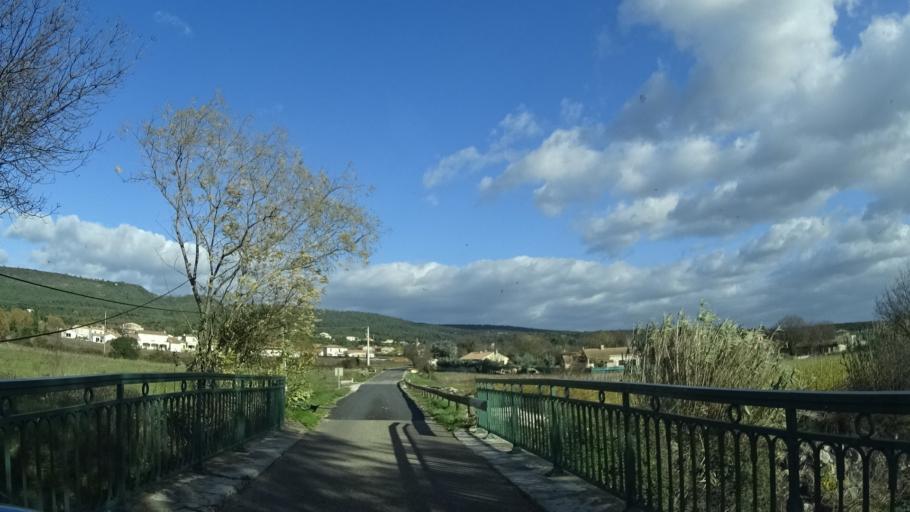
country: FR
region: Languedoc-Roussillon
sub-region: Departement de l'Herault
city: Claret
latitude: 43.8575
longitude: 3.8978
